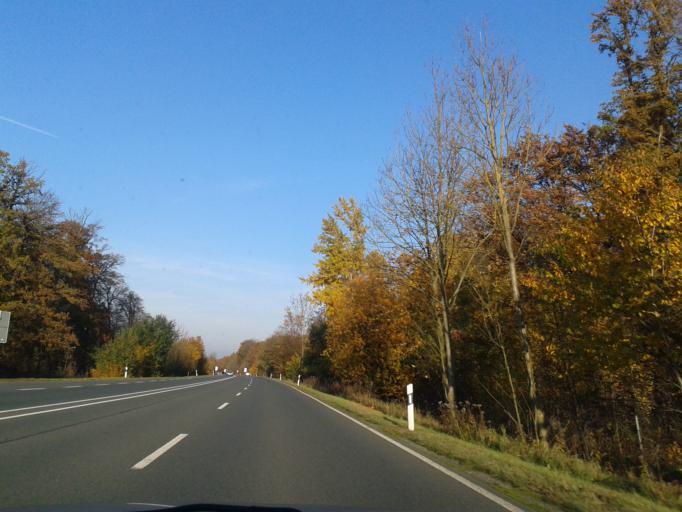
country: DE
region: North Rhine-Westphalia
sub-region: Regierungsbezirk Detmold
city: Salzkotten
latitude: 51.6301
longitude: 8.6415
